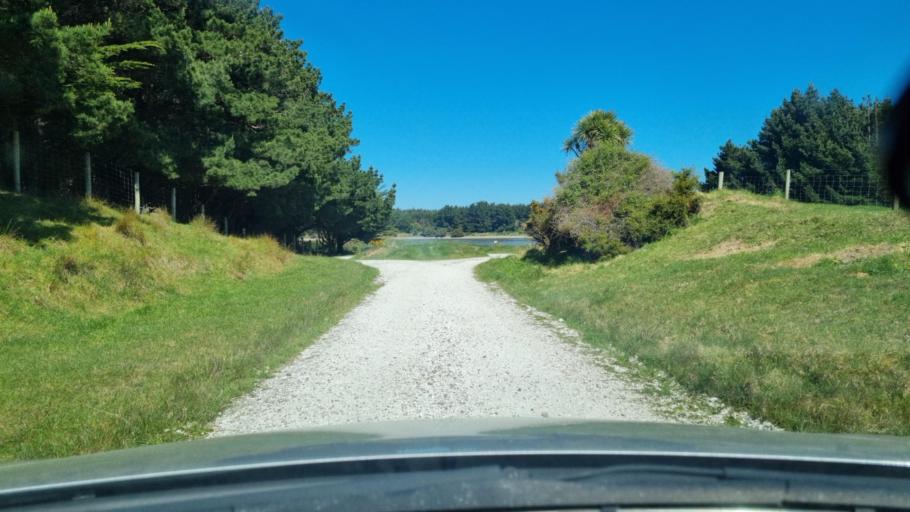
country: NZ
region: Southland
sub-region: Invercargill City
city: Invercargill
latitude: -46.4582
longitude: 168.2706
